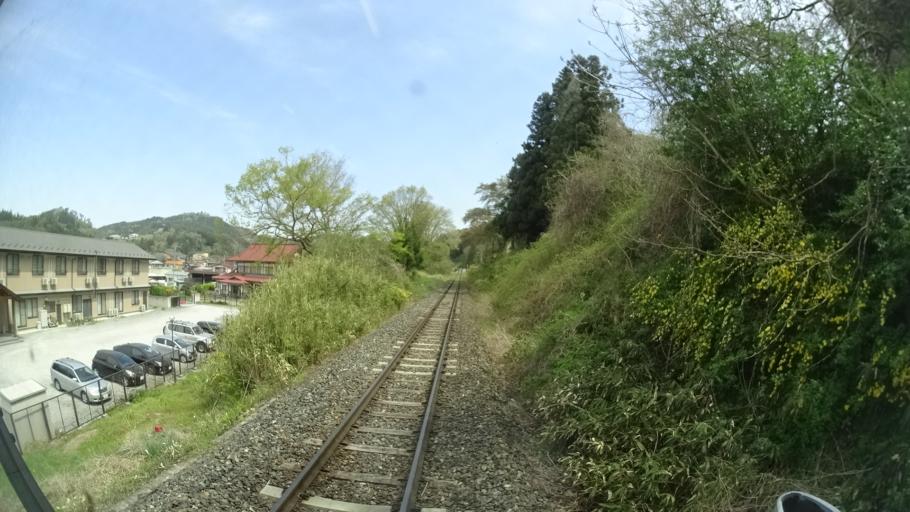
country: JP
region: Iwate
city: Ichinoseki
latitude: 38.9891
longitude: 141.2536
